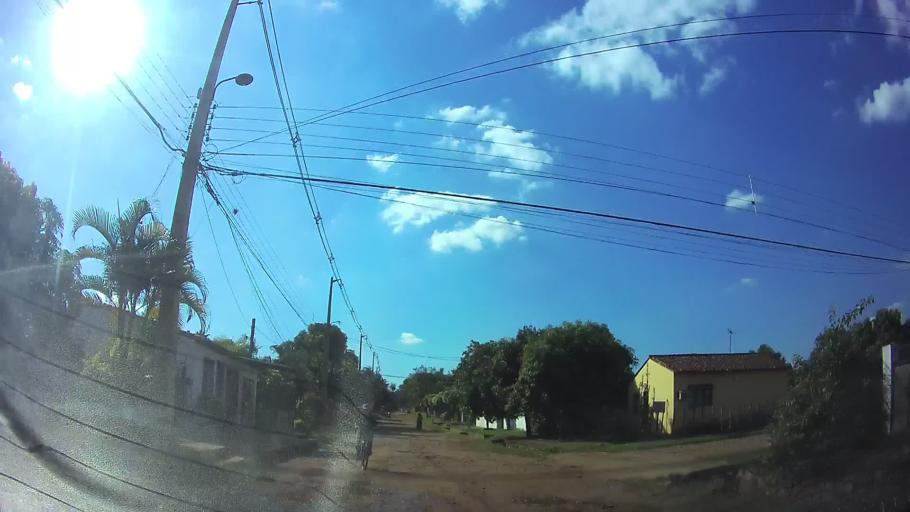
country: PY
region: Central
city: Limpio
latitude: -25.2544
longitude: -57.4749
